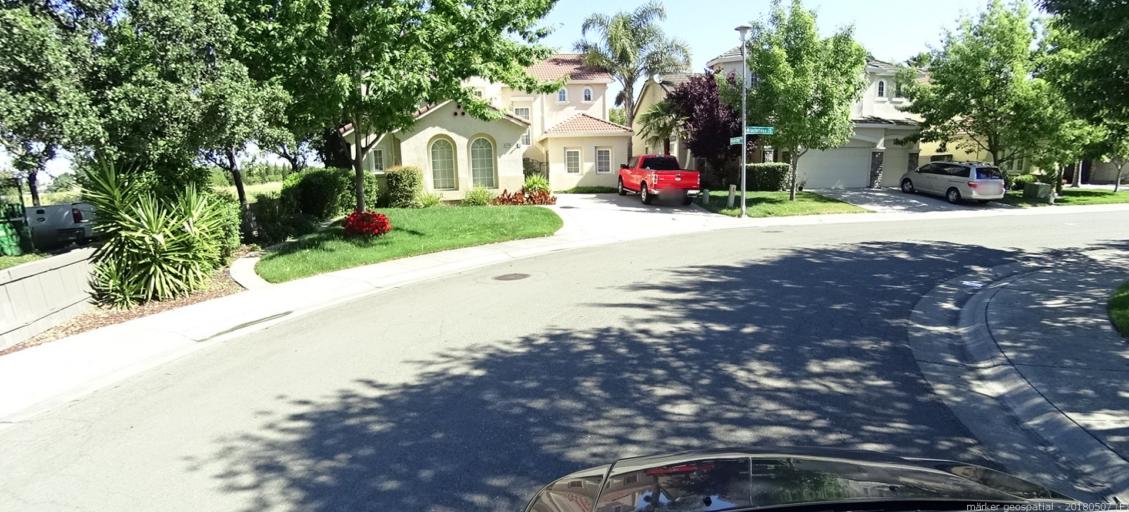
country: US
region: California
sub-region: Sacramento County
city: Rio Linda
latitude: 38.6636
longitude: -121.5067
